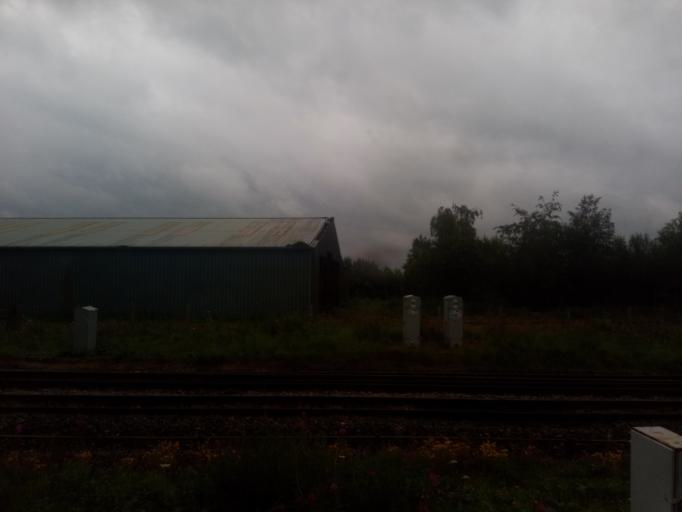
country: GB
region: England
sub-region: North Yorkshire
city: Settle
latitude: 54.0123
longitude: -2.2313
